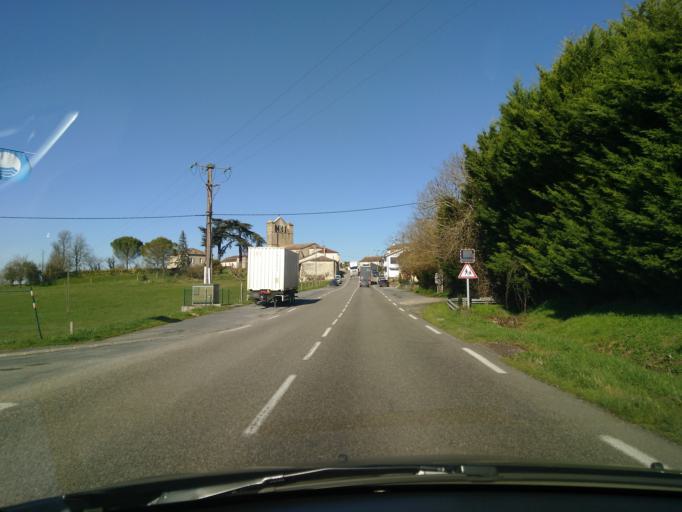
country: FR
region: Aquitaine
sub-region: Departement du Lot-et-Garonne
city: Cancon
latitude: 44.5813
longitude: 0.6238
